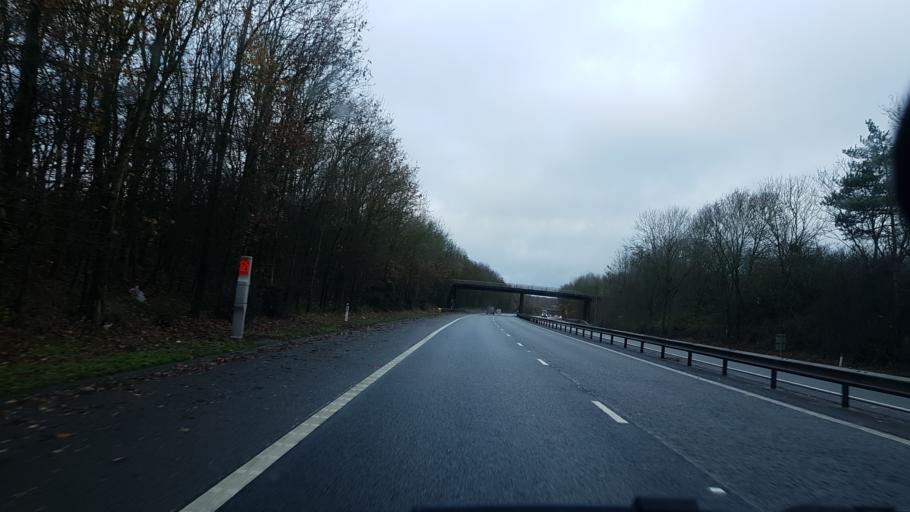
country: GB
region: England
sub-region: Bracknell Forest
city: Binfield
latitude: 51.4170
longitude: -0.8069
